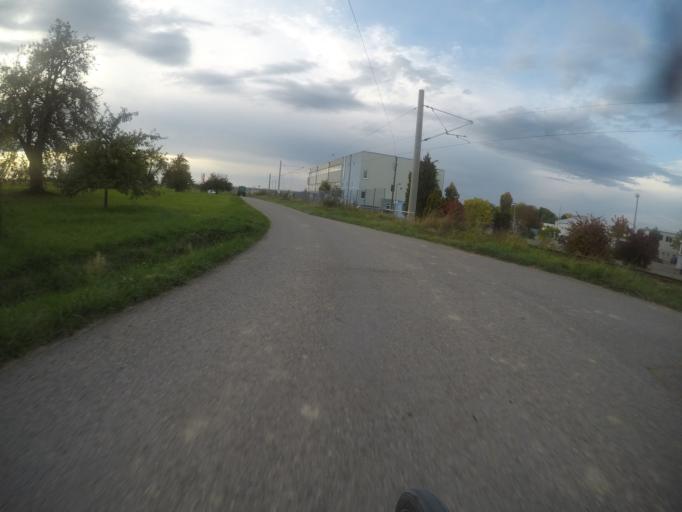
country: DE
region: Baden-Wuerttemberg
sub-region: Regierungsbezirk Stuttgart
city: Holzgerlingen
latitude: 48.6273
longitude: 9.0215
